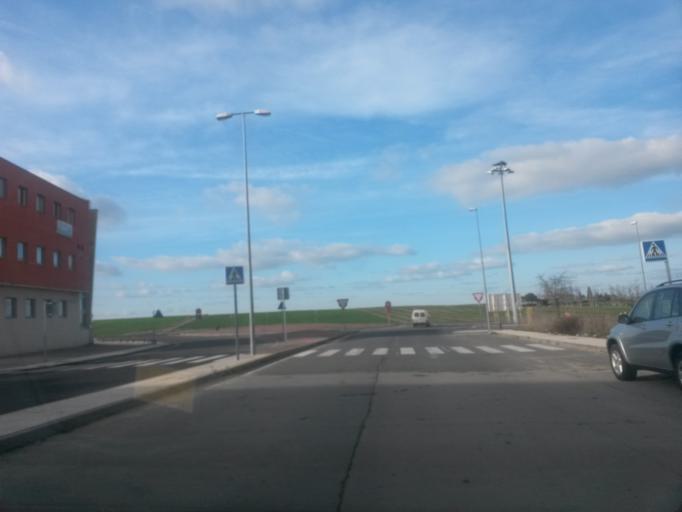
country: ES
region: Castille and Leon
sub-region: Provincia de Salamanca
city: San Cristobal de la Cuesta
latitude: 41.0096
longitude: -5.6103
